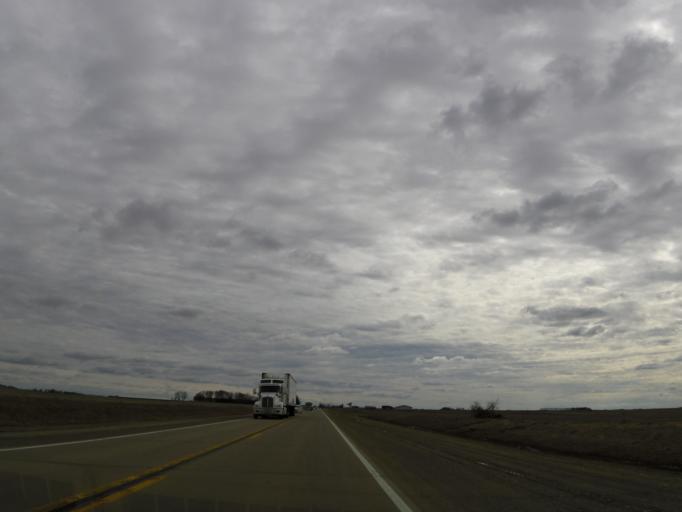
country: US
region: Iowa
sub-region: Howard County
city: Cresco
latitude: 43.4285
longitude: -92.2986
